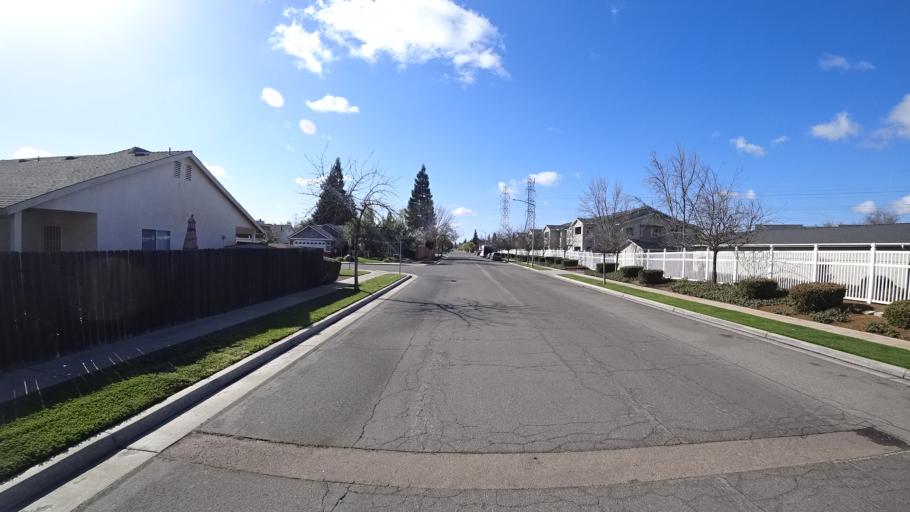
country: US
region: California
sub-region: Fresno County
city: West Park
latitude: 36.8234
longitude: -119.8806
